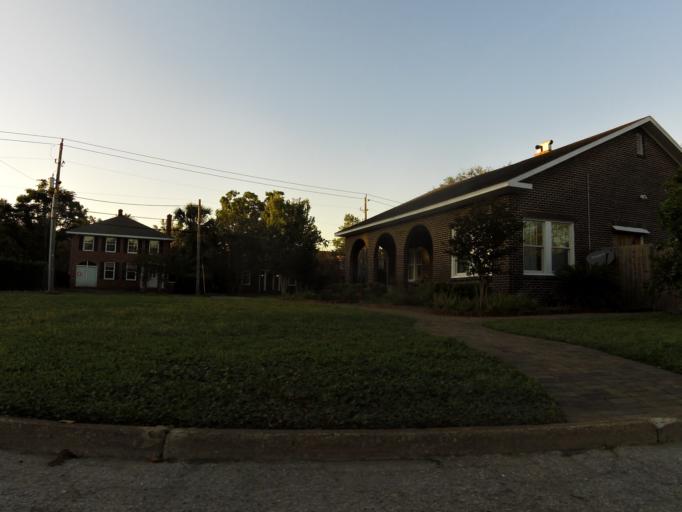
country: US
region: Florida
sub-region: Duval County
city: Jacksonville
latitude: 30.3057
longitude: -81.6572
